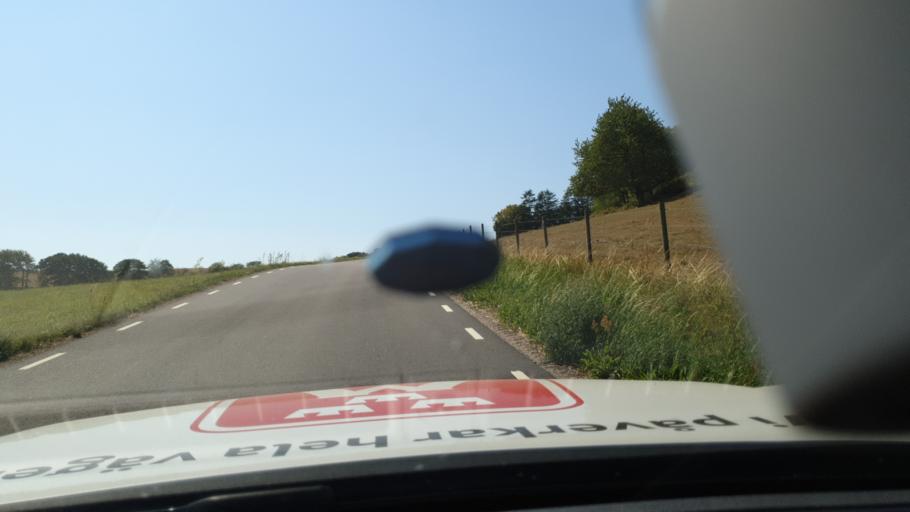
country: SE
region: Skane
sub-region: Sjobo Kommun
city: Blentarp
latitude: 55.5620
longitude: 13.5699
